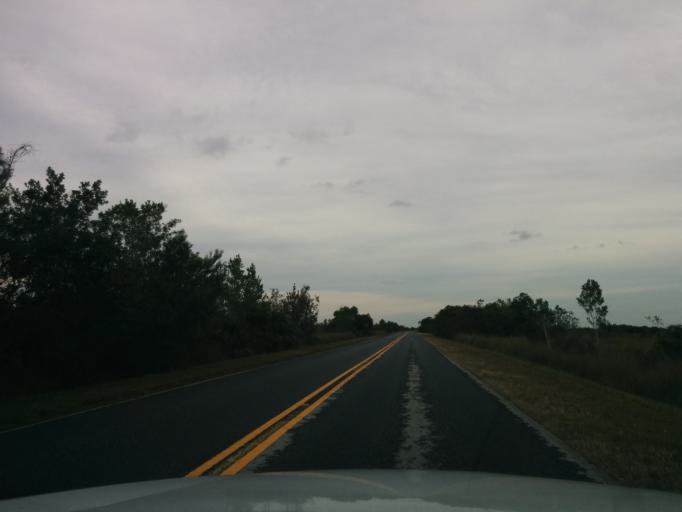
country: US
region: Florida
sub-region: Miami-Dade County
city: Florida City
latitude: 25.4345
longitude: -80.7250
